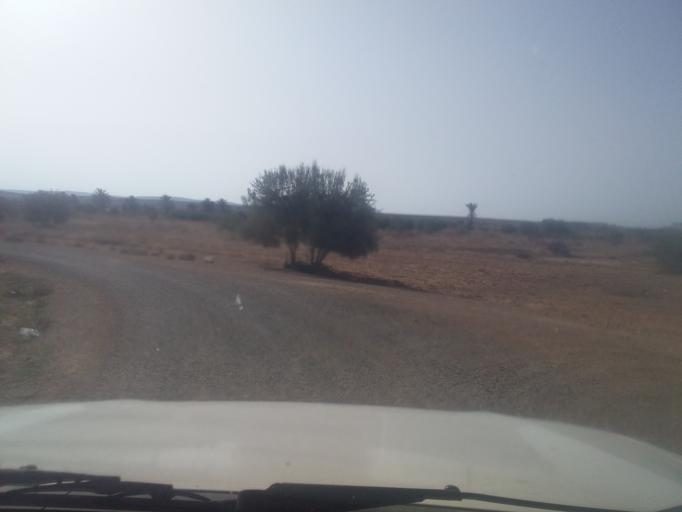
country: TN
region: Qabis
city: Matmata
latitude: 33.5850
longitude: 10.2587
